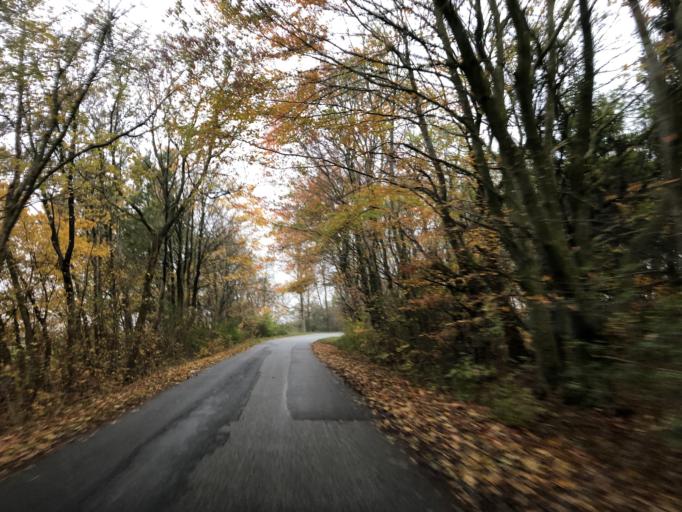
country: DK
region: Central Jutland
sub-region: Herning Kommune
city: Vildbjerg
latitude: 56.2205
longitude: 8.7696
